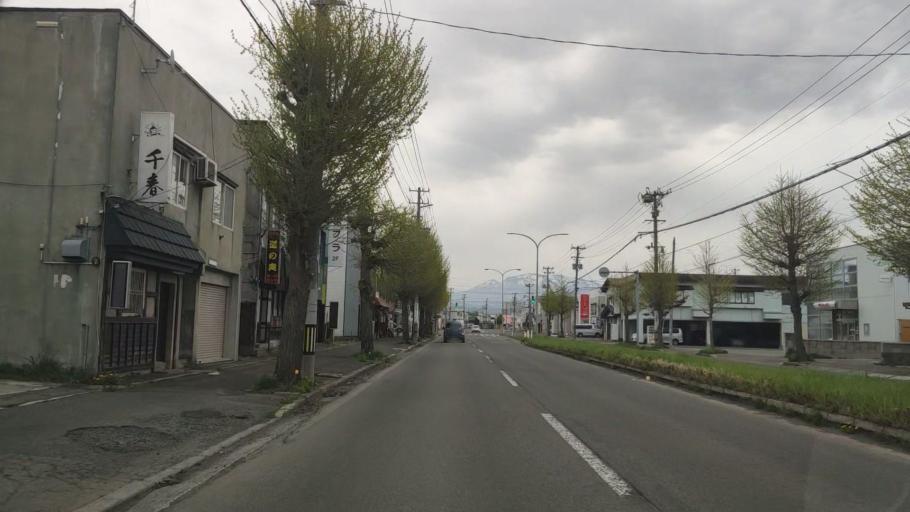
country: JP
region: Aomori
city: Aomori Shi
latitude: 40.8195
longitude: 140.7730
